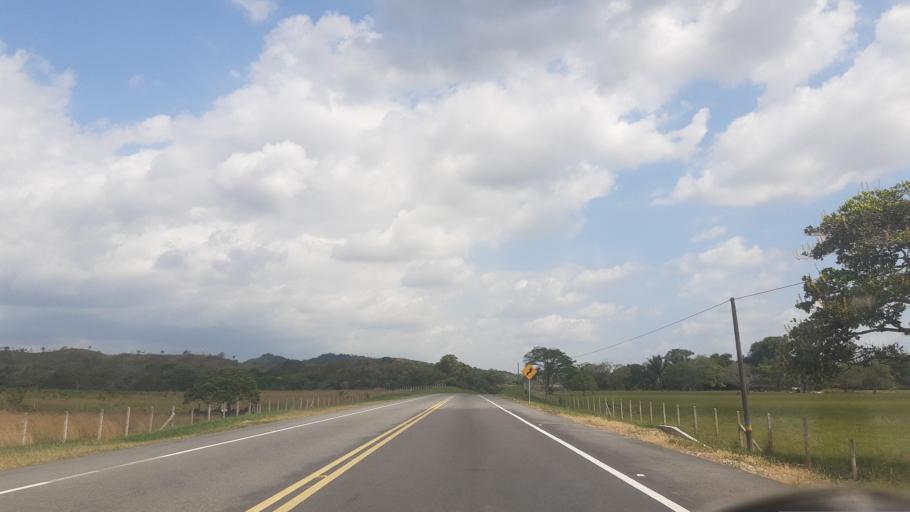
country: CO
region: Casanare
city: Tauramena
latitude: 4.8487
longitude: -72.7222
